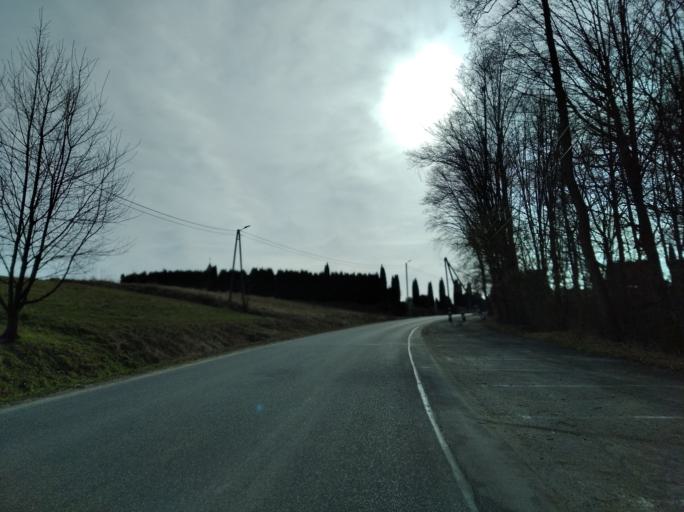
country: PL
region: Subcarpathian Voivodeship
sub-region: Powiat brzozowski
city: Jasienica Rosielna
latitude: 49.7467
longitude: 21.9418
